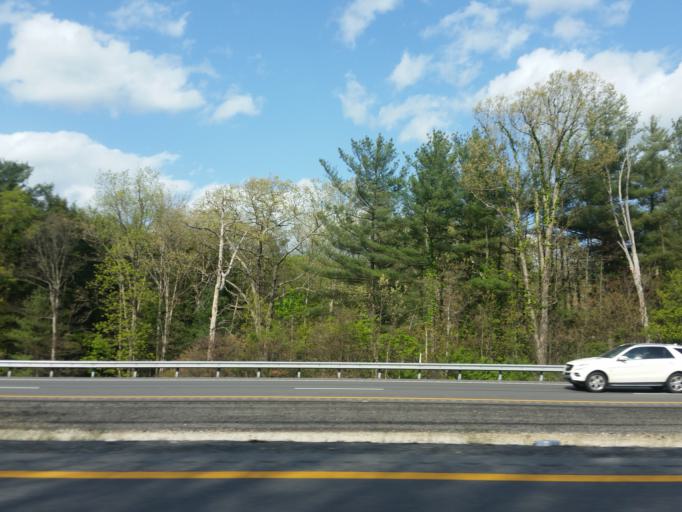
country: US
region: West Virginia
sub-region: Raleigh County
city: Beaver
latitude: 37.7153
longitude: -81.1523
